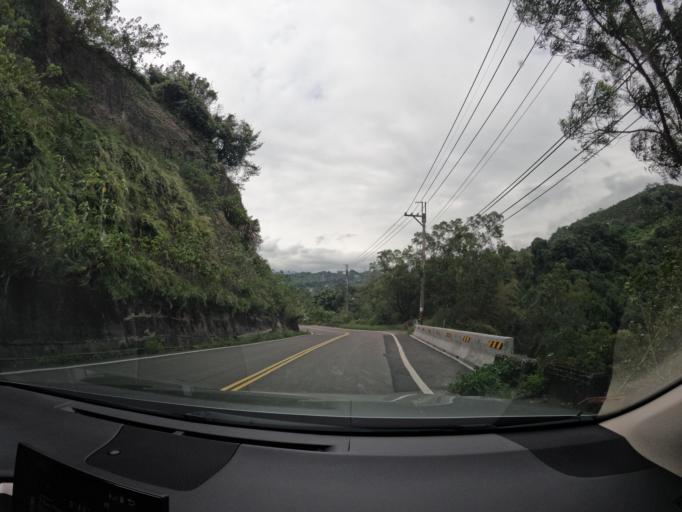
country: TW
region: Taiwan
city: Fengyuan
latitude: 24.3430
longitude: 120.8730
